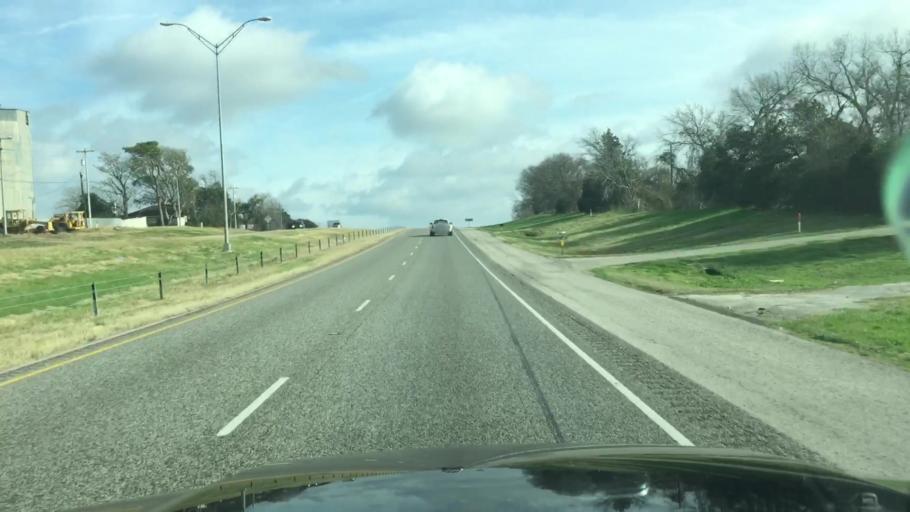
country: US
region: Texas
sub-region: Washington County
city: Brenham
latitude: 30.1405
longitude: -96.3576
